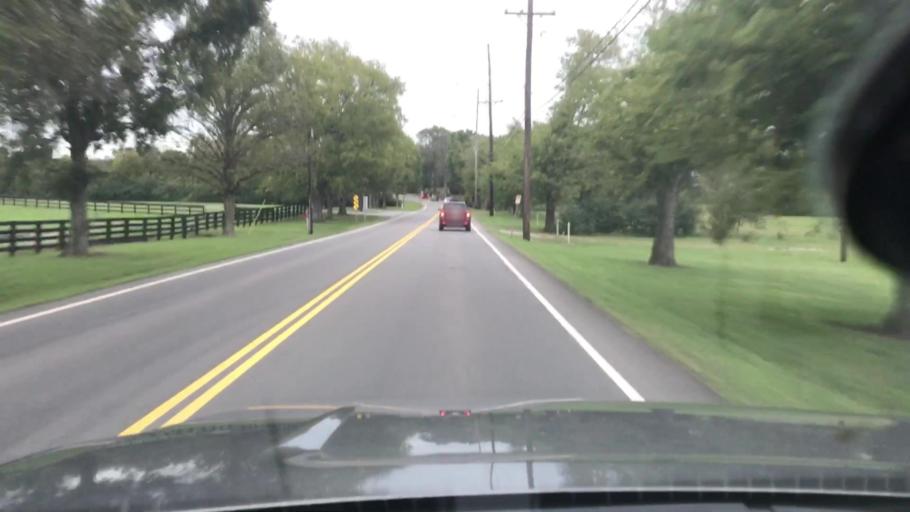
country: US
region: Tennessee
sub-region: Davidson County
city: Forest Hills
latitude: 36.0530
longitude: -86.8960
